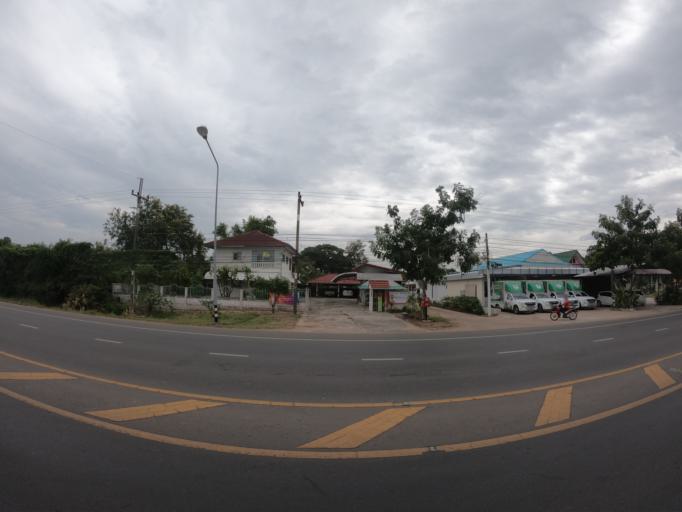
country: TH
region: Roi Et
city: Roi Et
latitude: 16.0785
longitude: 103.6920
